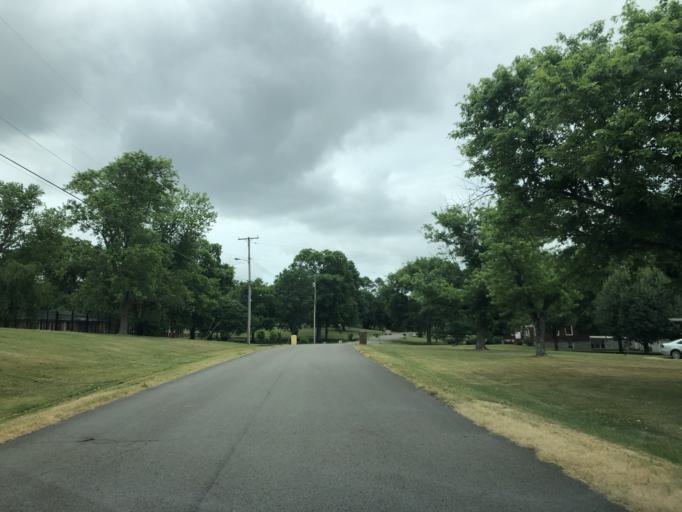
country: US
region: Tennessee
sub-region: Davidson County
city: Goodlettsville
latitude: 36.2671
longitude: -86.7625
